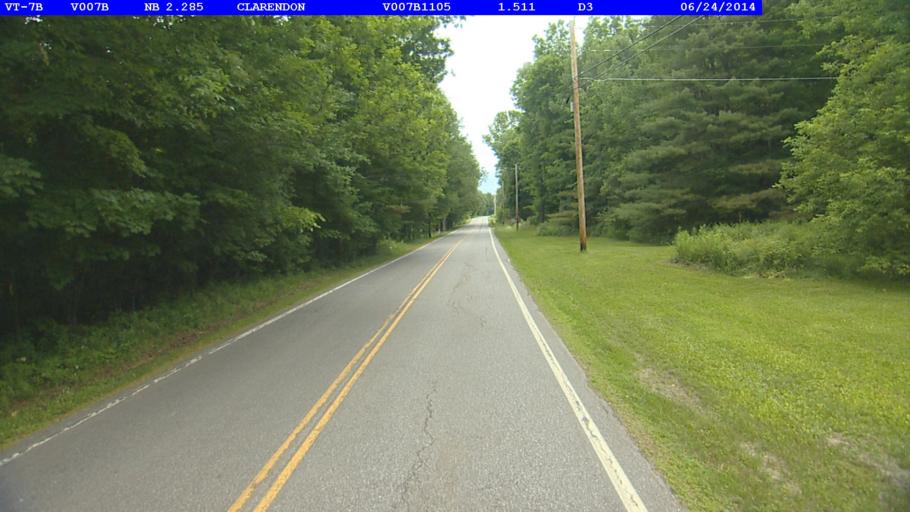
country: US
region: Vermont
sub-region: Rutland County
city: Rutland
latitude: 43.5230
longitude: -72.9612
